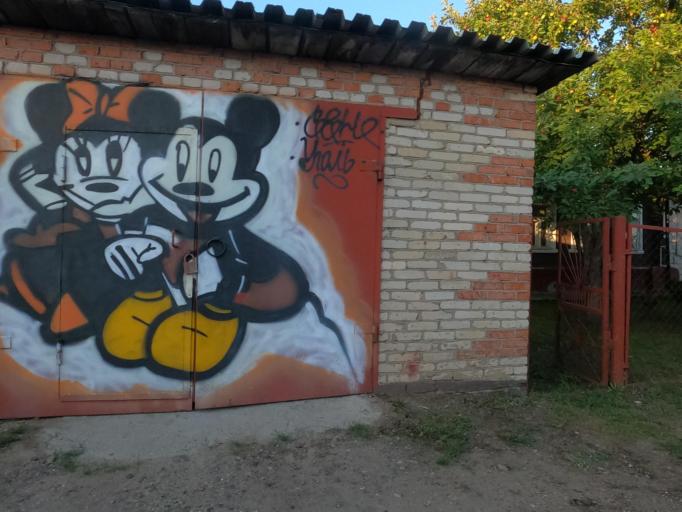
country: RU
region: Moskovskaya
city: Beloozerskiy
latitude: 55.4363
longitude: 38.4828
